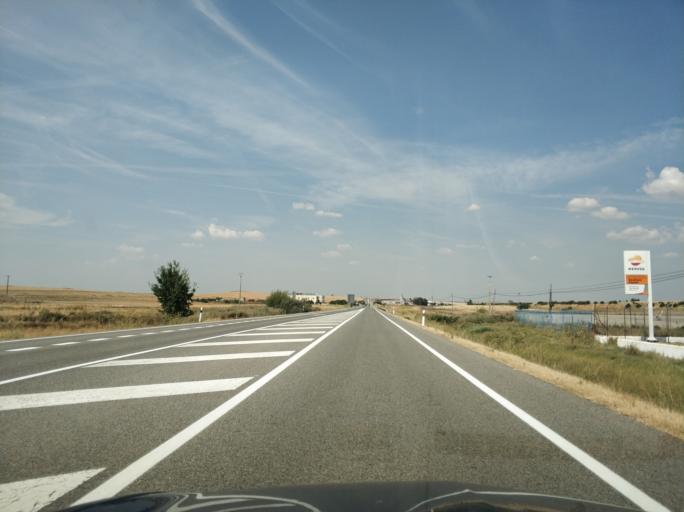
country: ES
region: Castille and Leon
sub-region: Provincia de Salamanca
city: Arapiles
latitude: 40.8967
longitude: -5.6644
